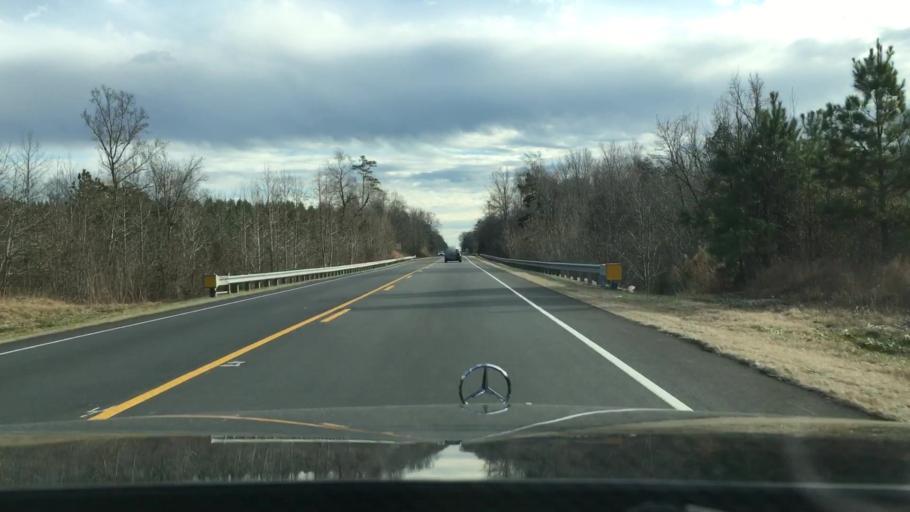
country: US
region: Virginia
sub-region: City of Danville
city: Danville
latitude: 36.4995
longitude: -79.3870
